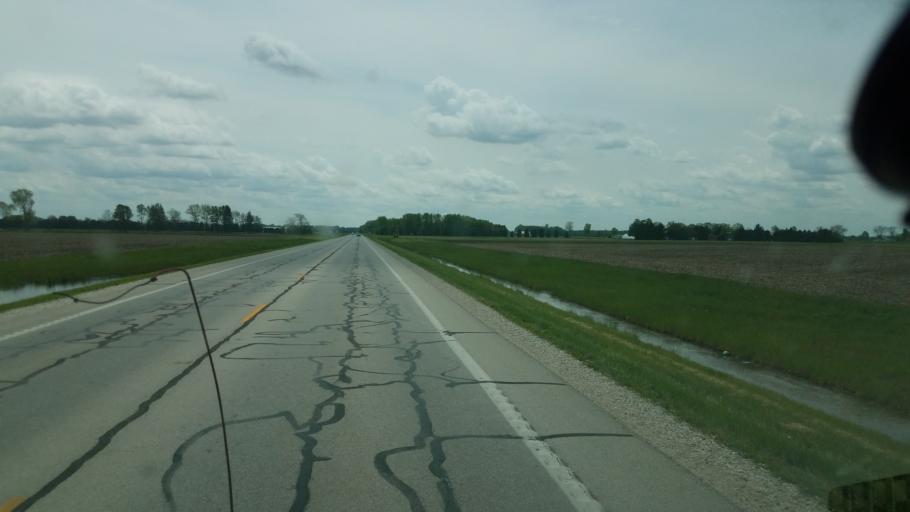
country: US
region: Ohio
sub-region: Sandusky County
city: Stony Prairie
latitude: 41.3164
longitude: -83.1683
